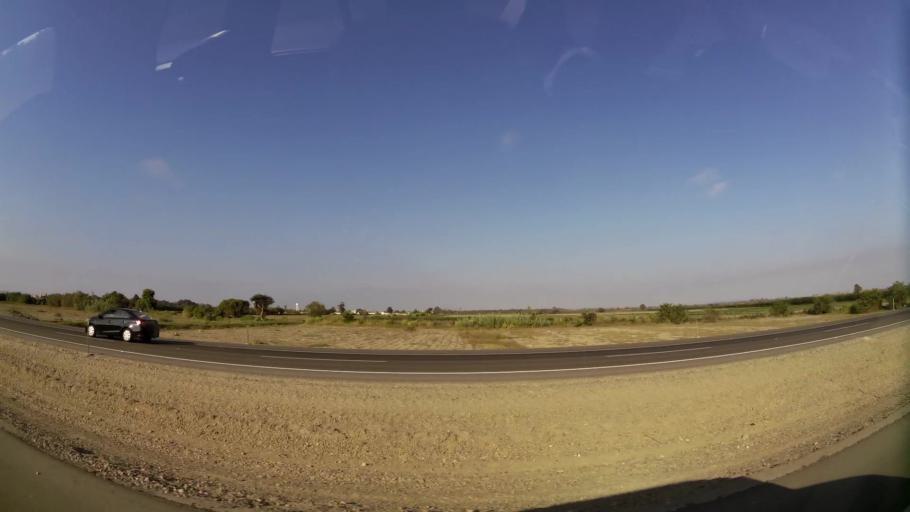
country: PE
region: Ica
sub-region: Provincia de Chincha
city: Chincha Baja
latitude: -13.4824
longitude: -76.1845
